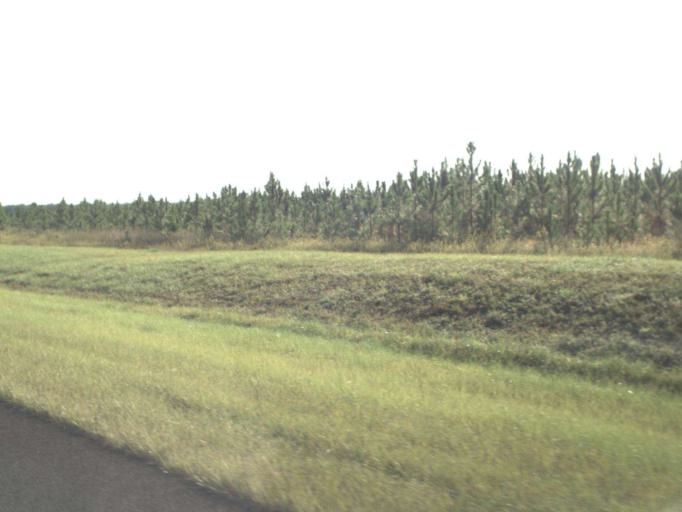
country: US
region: Florida
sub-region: Bay County
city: Laguna Beach
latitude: 30.4600
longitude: -85.8680
